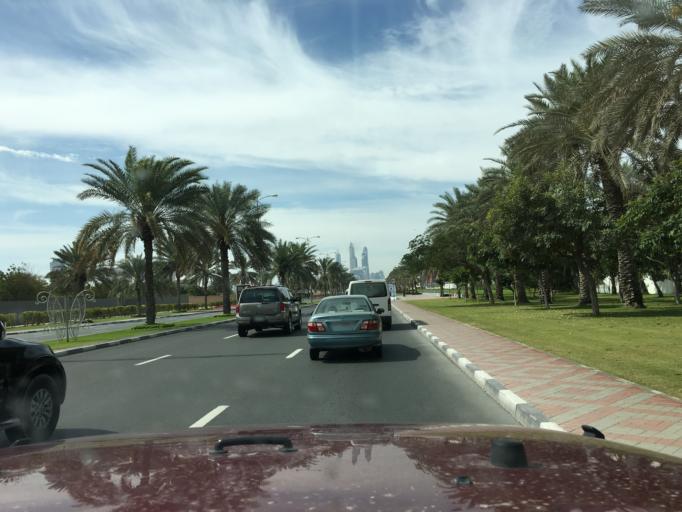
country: AE
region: Dubai
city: Dubai
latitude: 25.1231
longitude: 55.1792
